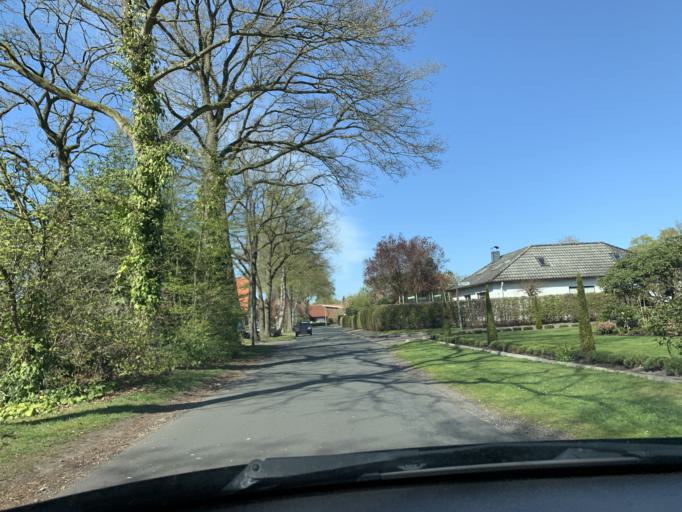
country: DE
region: Lower Saxony
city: Westerstede
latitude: 53.2476
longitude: 7.9406
